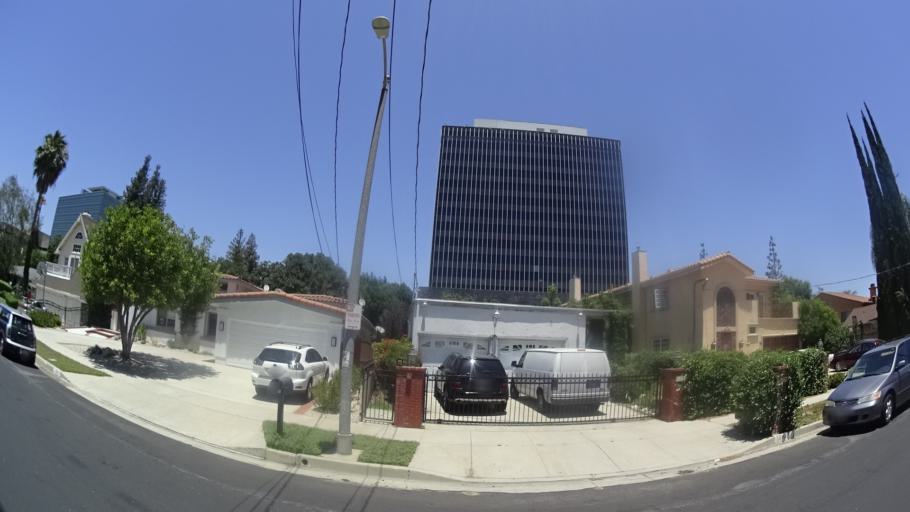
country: US
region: California
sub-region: Los Angeles County
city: Sherman Oaks
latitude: 34.1545
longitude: -118.4802
